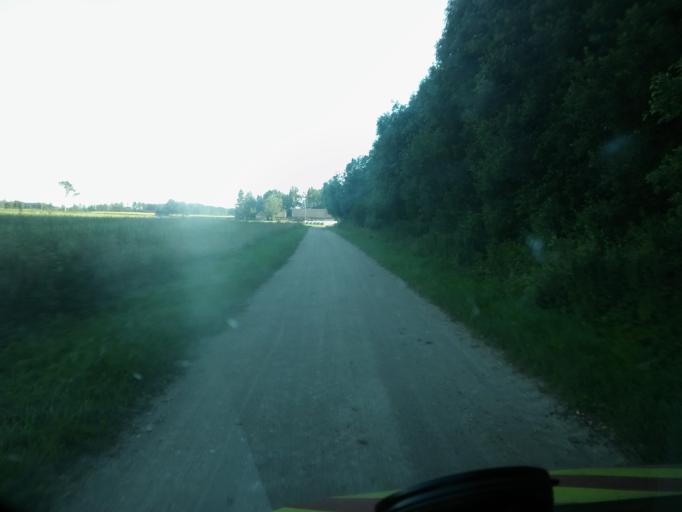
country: EE
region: Valgamaa
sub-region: Torva linn
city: Torva
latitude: 58.0885
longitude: 25.9938
